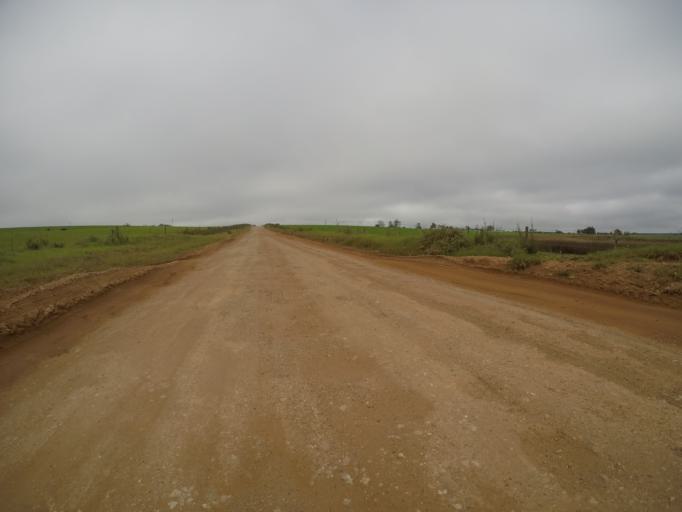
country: ZA
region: Eastern Cape
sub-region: Cacadu District Municipality
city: Kareedouw
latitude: -34.0281
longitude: 24.2428
